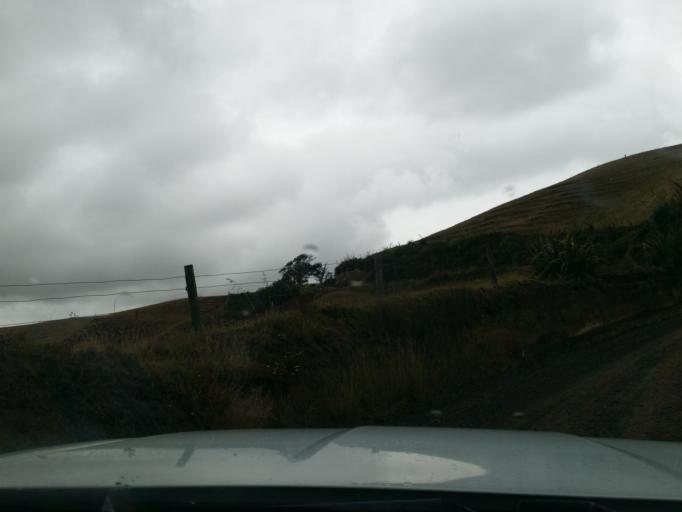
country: NZ
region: Northland
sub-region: Kaipara District
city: Dargaville
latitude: -36.0010
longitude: 173.7940
